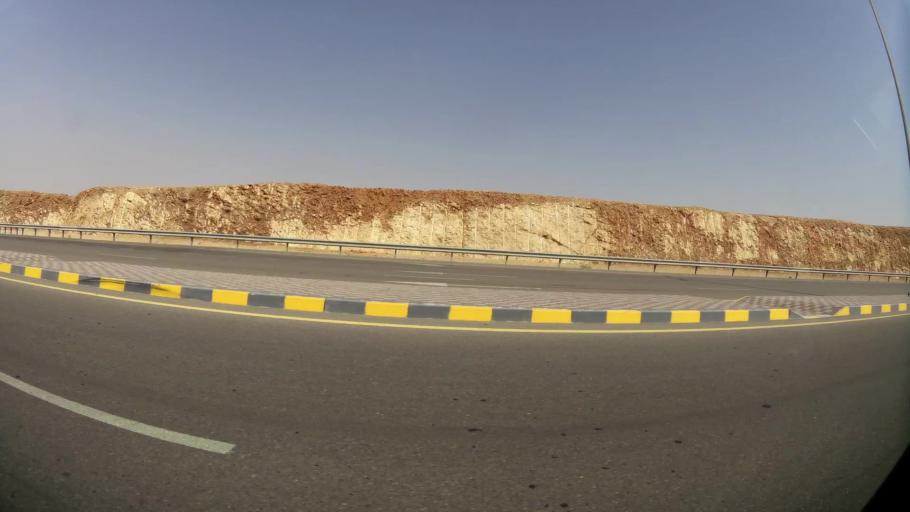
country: OM
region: Muhafazat Masqat
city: Bawshar
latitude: 23.5551
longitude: 58.3393
